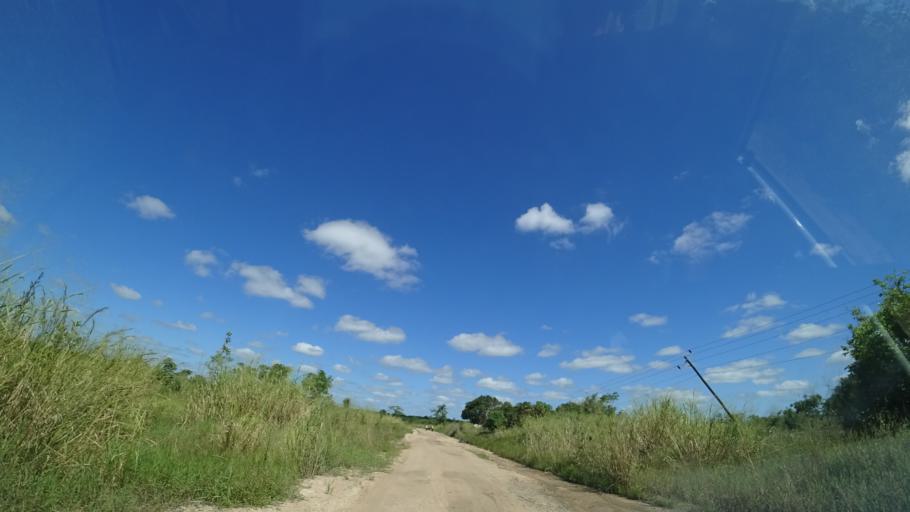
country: MZ
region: Sofala
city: Dondo
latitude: -19.3140
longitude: 34.6914
